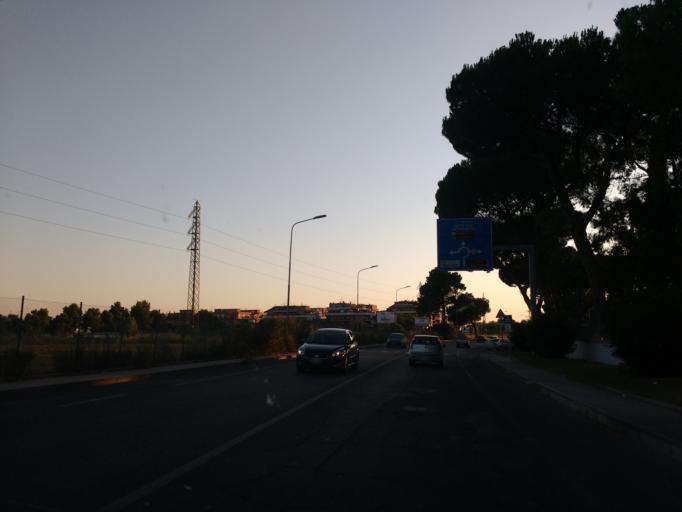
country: IT
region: Latium
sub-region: Citta metropolitana di Roma Capitale
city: Albuccione
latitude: 41.9524
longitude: 12.7002
